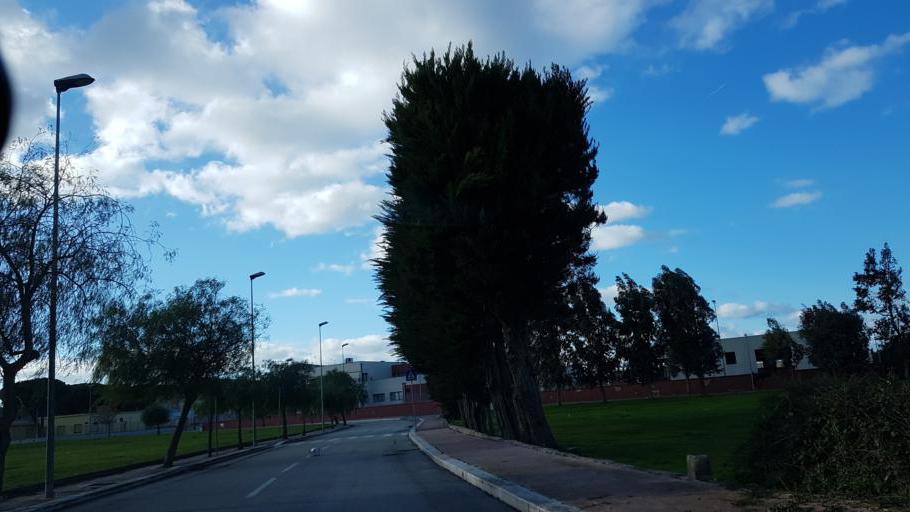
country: IT
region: Apulia
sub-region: Provincia di Brindisi
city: Brindisi
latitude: 40.6516
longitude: 17.9184
